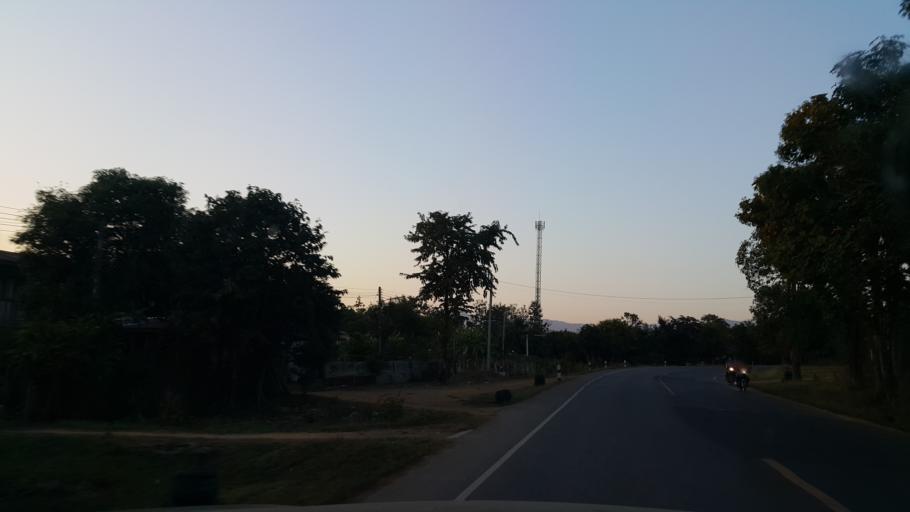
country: TH
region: Phrae
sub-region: Amphoe Wang Chin
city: Wang Chin
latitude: 17.8468
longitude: 99.6287
